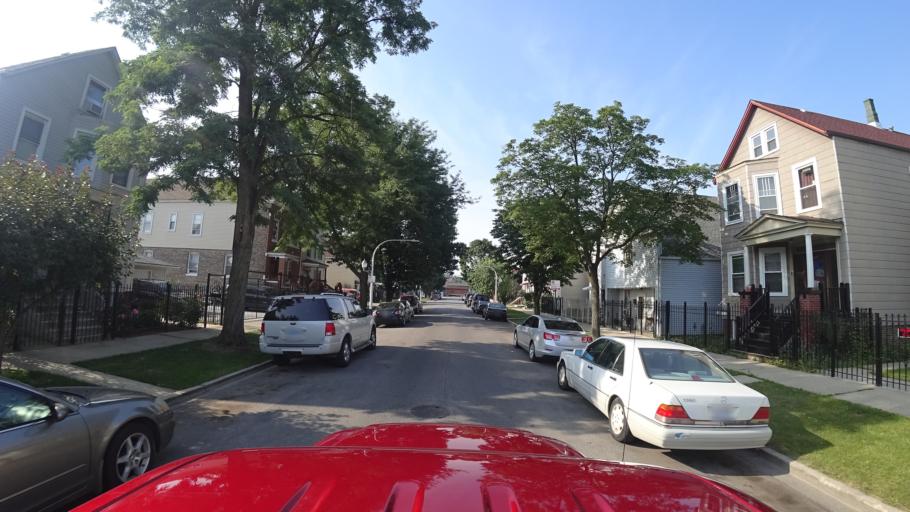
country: US
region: Illinois
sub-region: Cook County
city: Chicago
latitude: 41.8094
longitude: -87.6991
